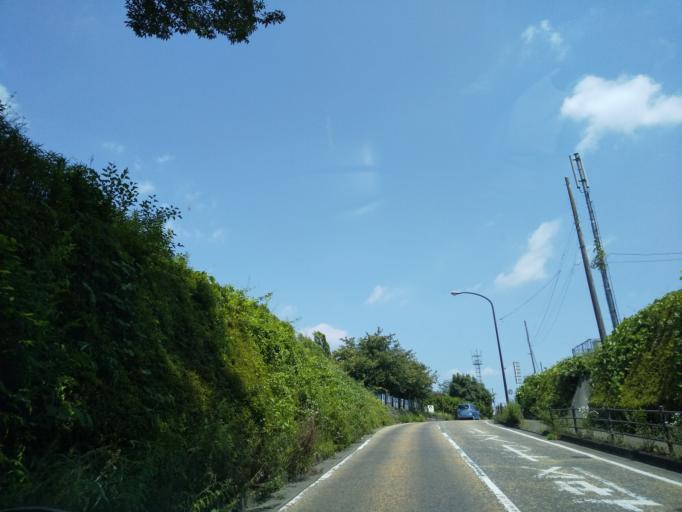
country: JP
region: Kanagawa
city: Zama
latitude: 35.5195
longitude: 139.3862
